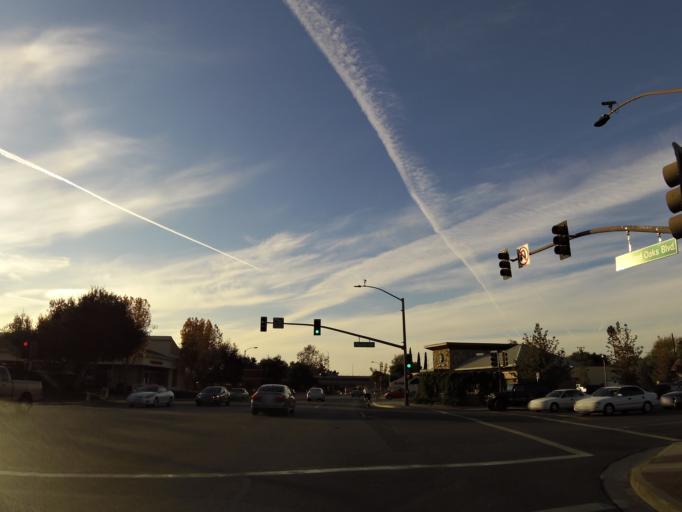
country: US
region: California
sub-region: Ventura County
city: Thousand Oaks
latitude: 34.1785
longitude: -118.8576
